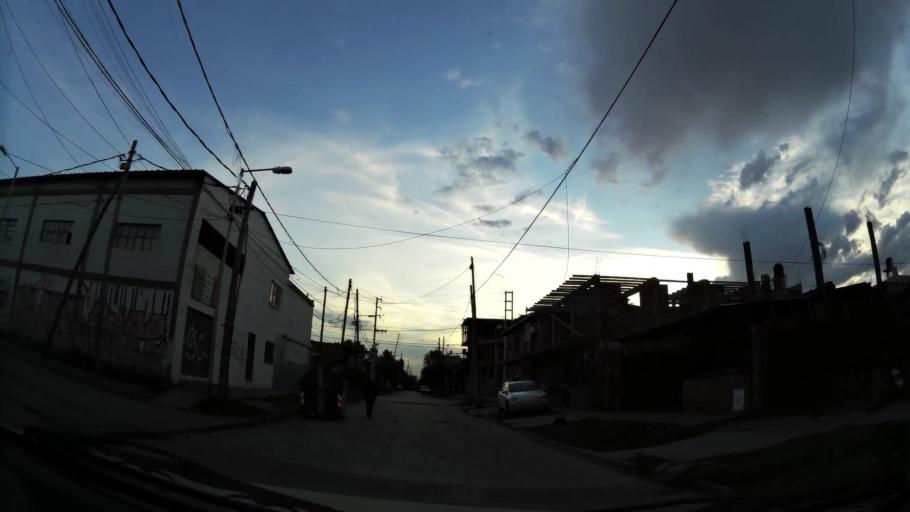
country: AR
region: Buenos Aires
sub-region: Partido de Avellaneda
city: Avellaneda
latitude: -34.6813
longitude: -58.3288
